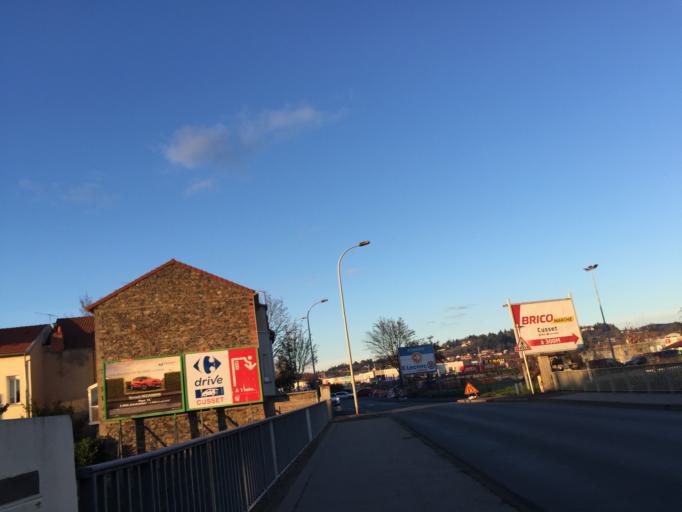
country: FR
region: Auvergne
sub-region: Departement de l'Allier
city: Vichy
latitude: 46.1340
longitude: 3.4317
